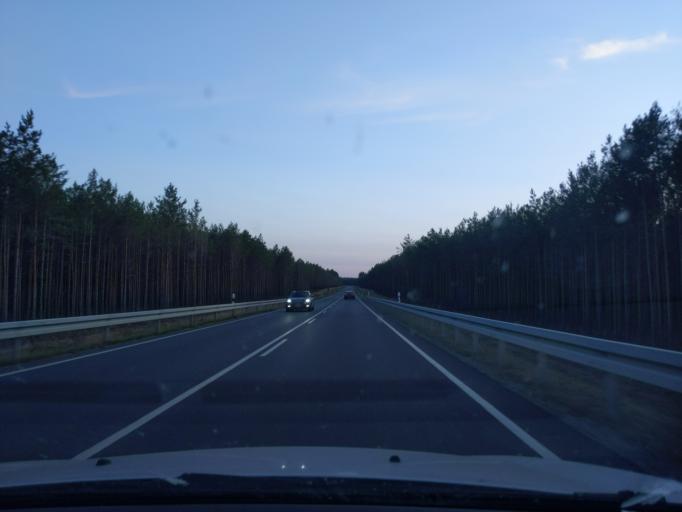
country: DE
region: Saxony
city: Hoyerswerda
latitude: 51.4210
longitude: 14.2952
